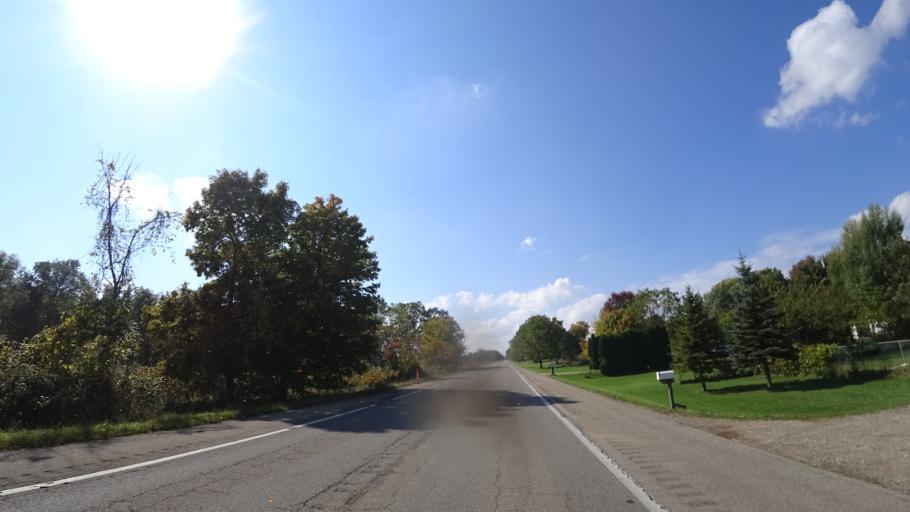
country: US
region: Michigan
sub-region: Calhoun County
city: Homer
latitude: 42.1330
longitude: -84.8791
